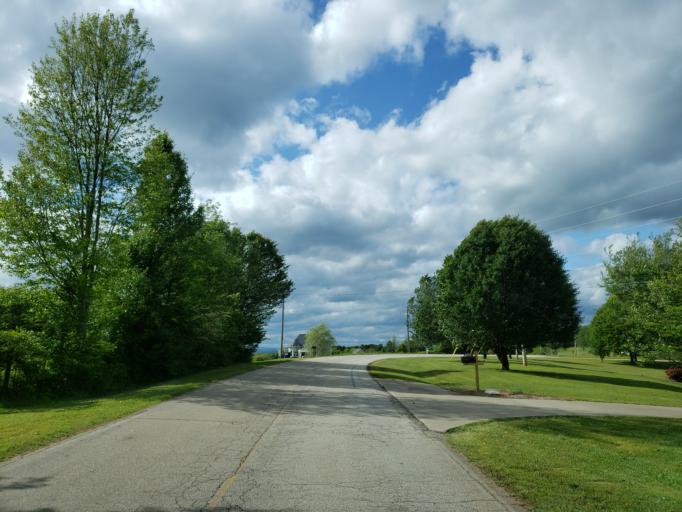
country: US
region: Georgia
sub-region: Haralson County
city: Tallapoosa
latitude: 33.6729
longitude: -85.2903
